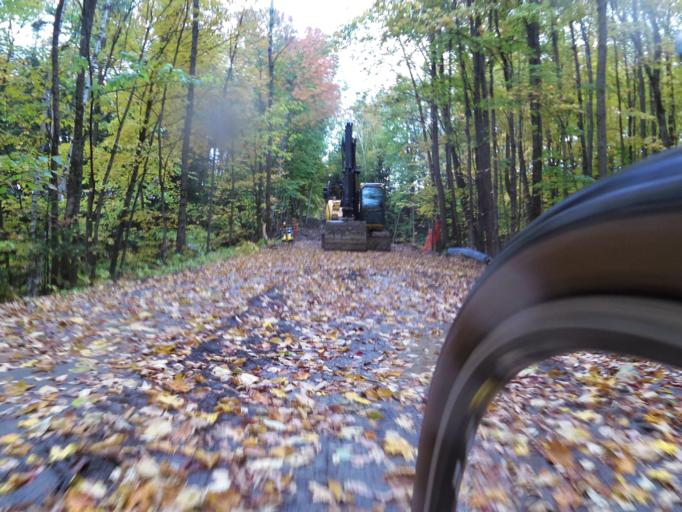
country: CA
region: Quebec
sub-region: Outaouais
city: Shawville
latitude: 45.6899
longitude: -76.5652
